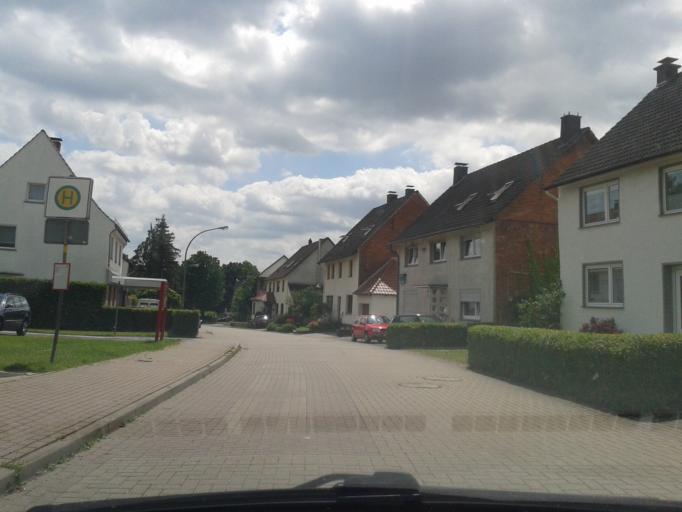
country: DE
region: North Rhine-Westphalia
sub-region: Regierungsbezirk Detmold
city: Steinheim
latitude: 51.8985
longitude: 9.0563
